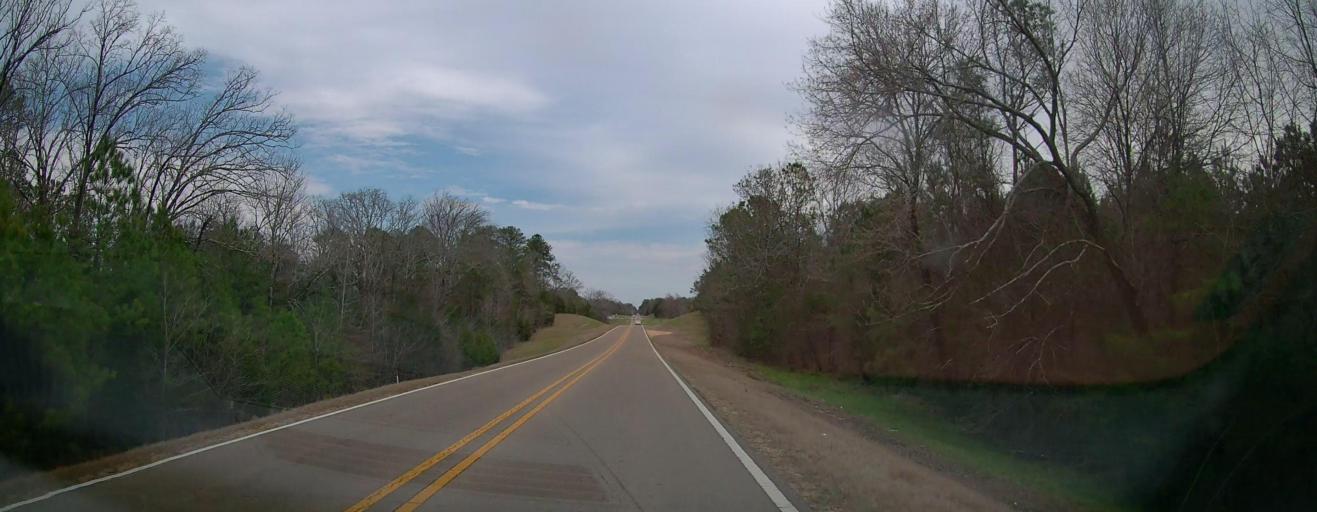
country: US
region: Mississippi
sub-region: Itawamba County
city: Mantachie
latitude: 34.2621
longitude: -88.5294
